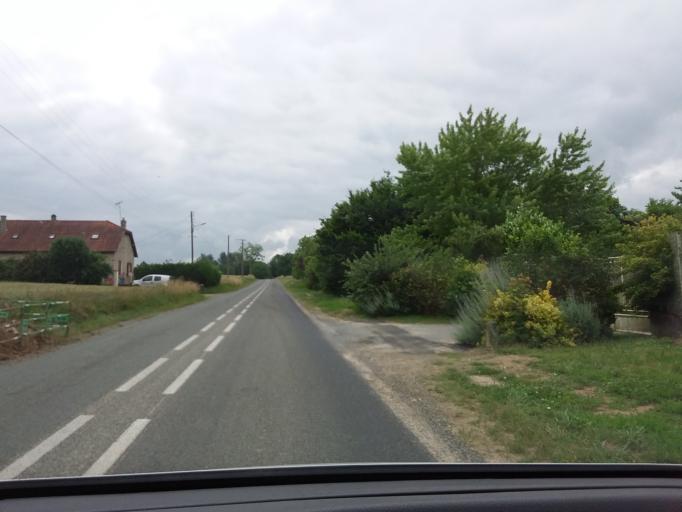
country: FR
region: Picardie
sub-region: Departement de l'Aisne
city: Vailly-sur-Aisne
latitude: 49.4043
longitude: 3.5551
